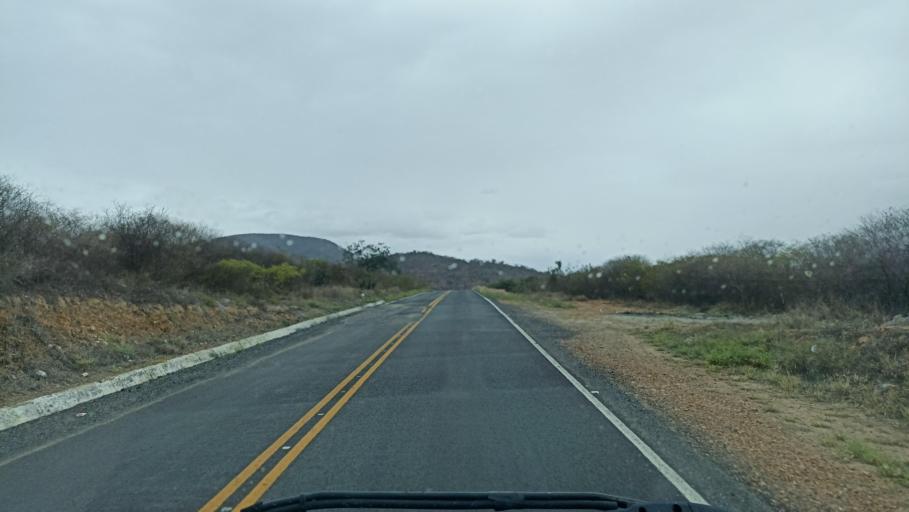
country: BR
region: Bahia
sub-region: Andarai
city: Vera Cruz
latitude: -13.0462
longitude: -40.7685
